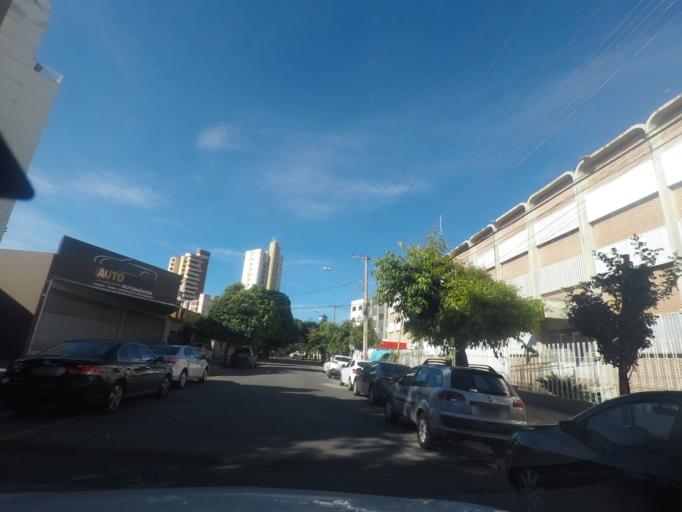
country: BR
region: Goias
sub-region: Goiania
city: Goiania
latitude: -16.6724
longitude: -49.2704
